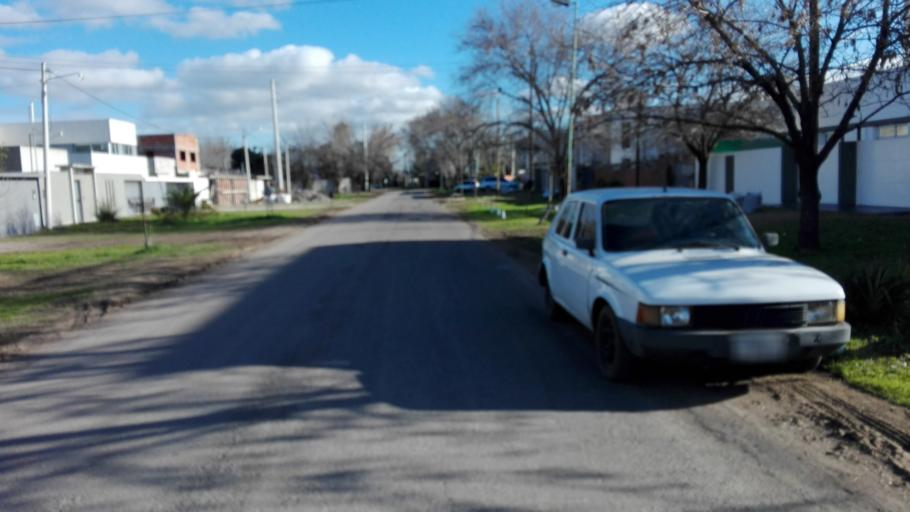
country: AR
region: Buenos Aires
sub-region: Partido de La Plata
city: La Plata
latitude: -34.9048
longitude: -58.0230
